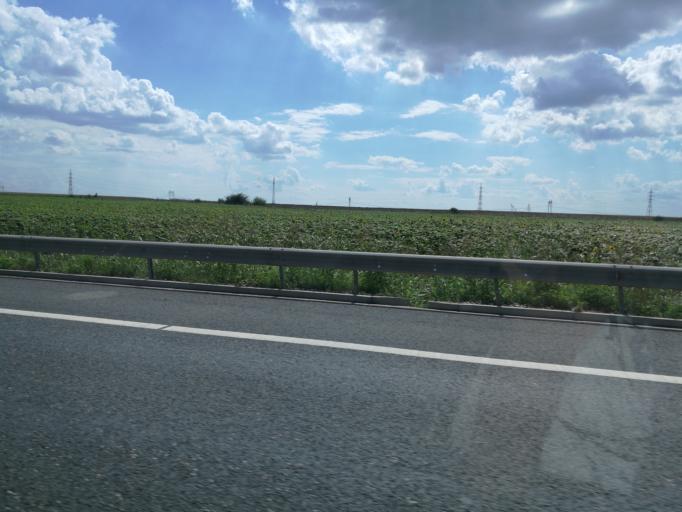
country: RO
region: Constanta
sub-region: Comuna Ovidiu
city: Ovidiu
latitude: 44.2403
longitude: 28.5481
